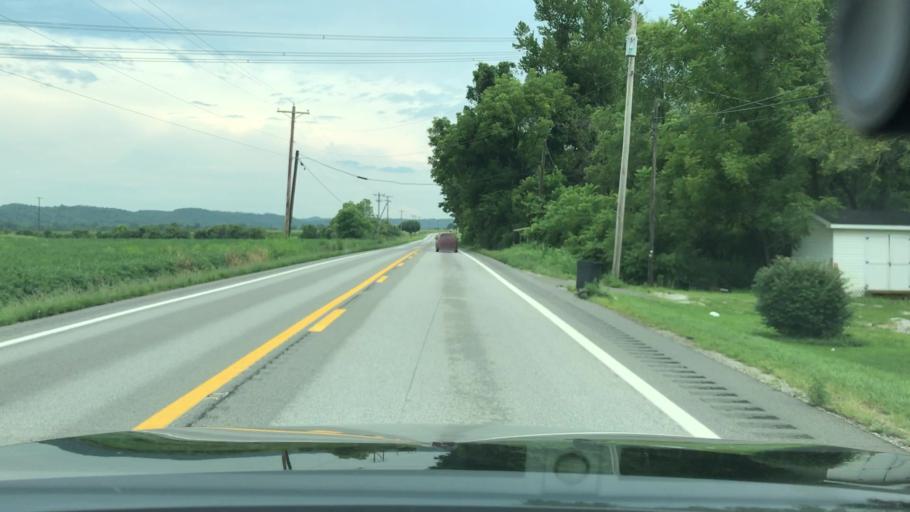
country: US
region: West Virginia
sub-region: Putnam County
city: Buffalo
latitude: 38.7436
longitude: -81.9800
